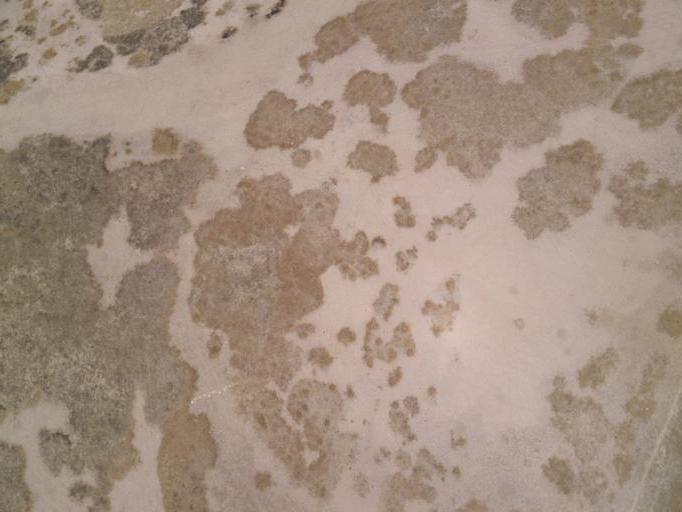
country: BO
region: La Paz
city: Batallas
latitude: -16.3511
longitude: -68.6318
